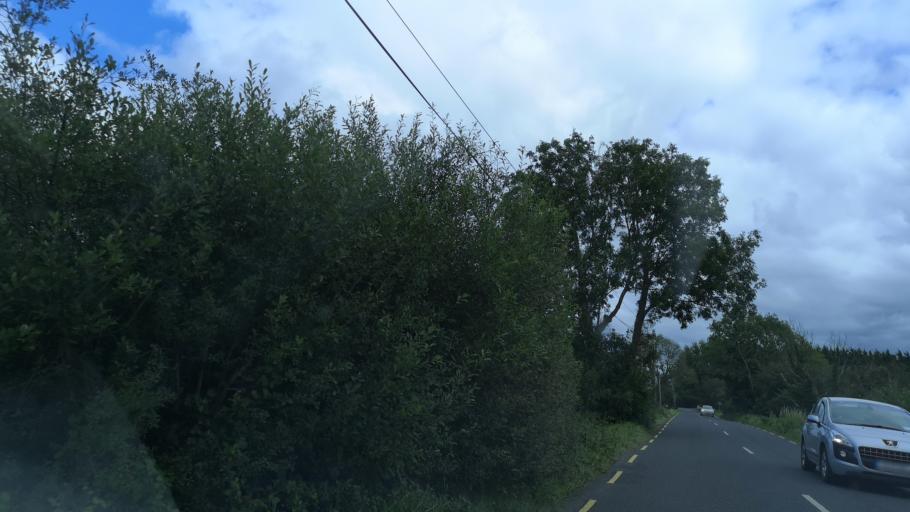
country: IE
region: Leinster
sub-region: Uibh Fhaili
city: Ferbane
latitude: 53.2249
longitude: -7.8315
